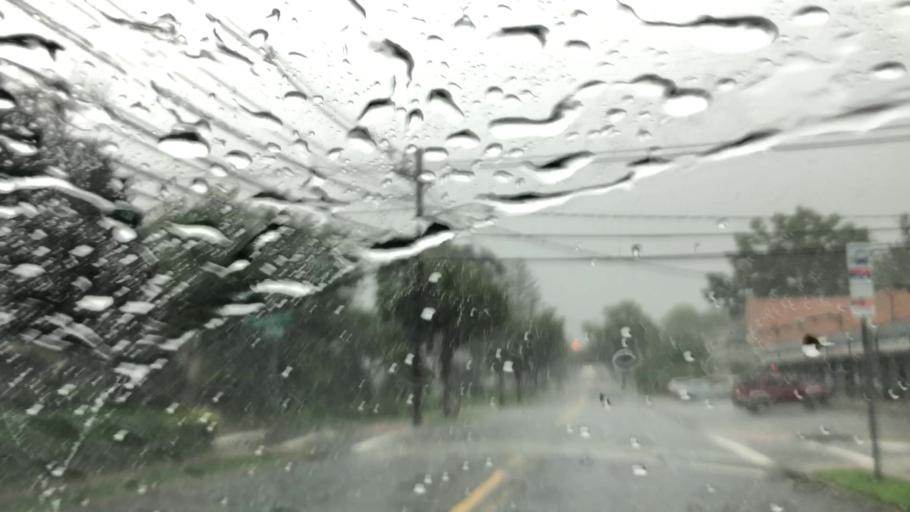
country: US
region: New Jersey
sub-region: Bergen County
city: Rochelle Park
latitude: 40.9060
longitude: -74.0767
